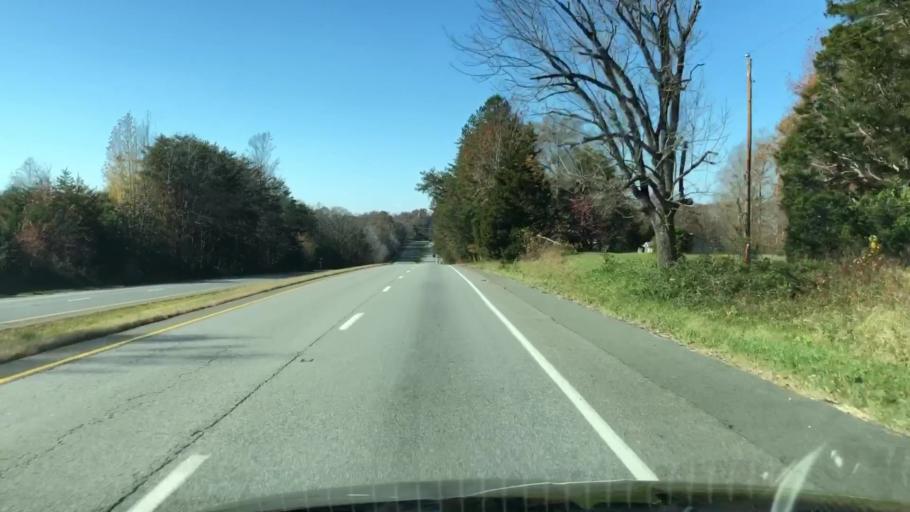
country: US
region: Virginia
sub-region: Stafford County
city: Falmouth
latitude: 38.4076
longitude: -77.5905
